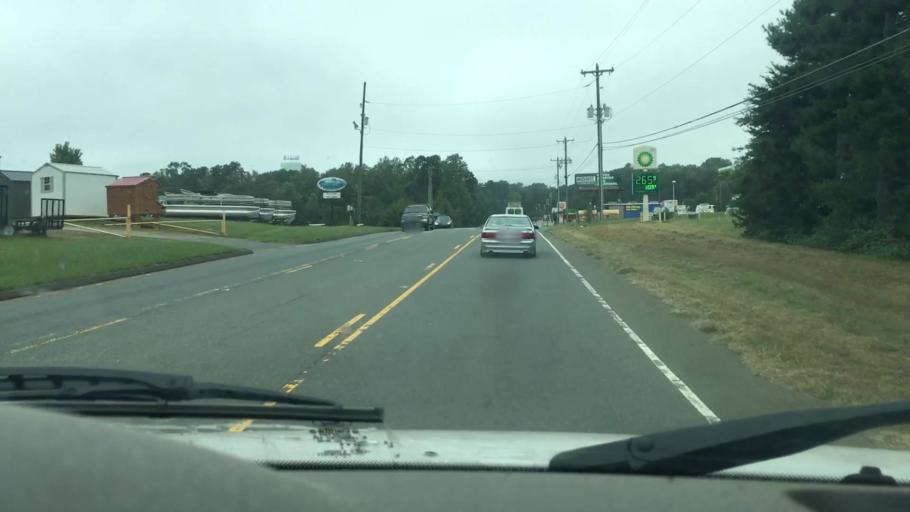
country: US
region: North Carolina
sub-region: Catawba County
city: Lake Norman of Catawba
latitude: 35.6030
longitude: -80.9118
